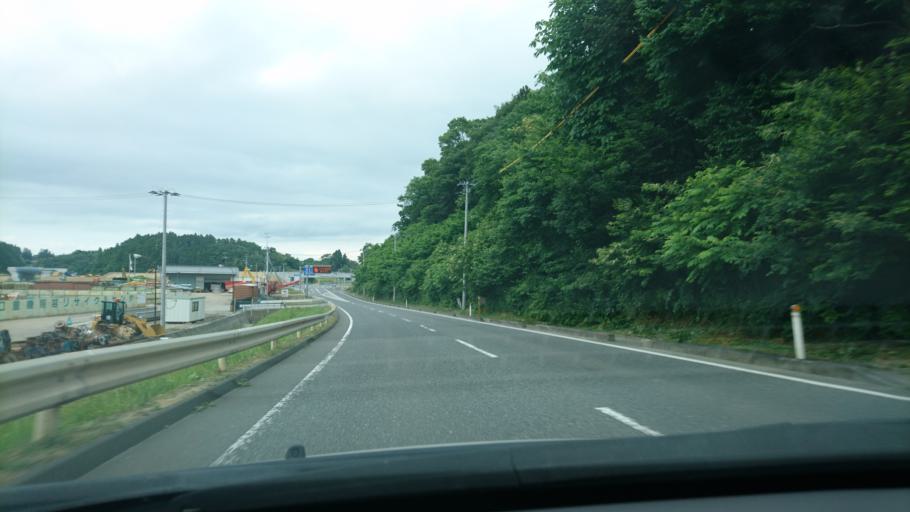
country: JP
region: Miyagi
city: Kogota
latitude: 38.7292
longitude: 141.0532
